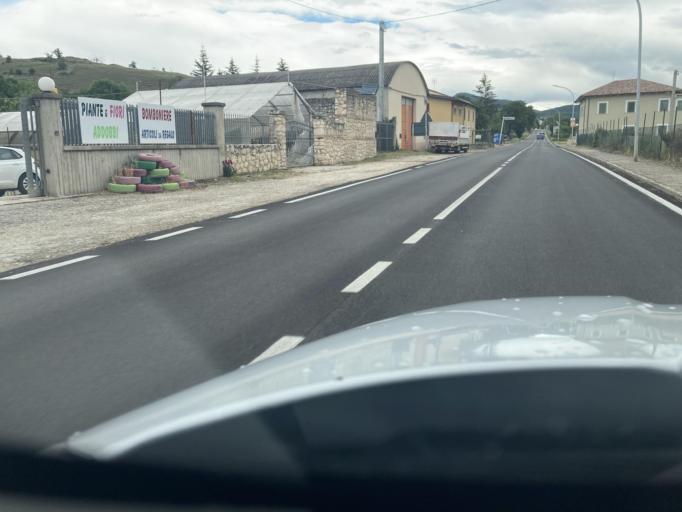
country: IT
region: Abruzzo
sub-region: Provincia dell' Aquila
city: Sant'Eusanio Forconese
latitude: 42.2953
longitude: 13.5362
